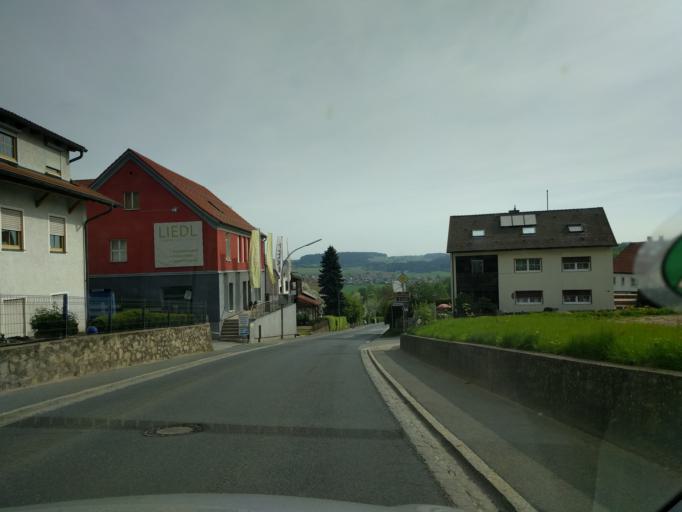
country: DE
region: Bavaria
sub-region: Upper Palatinate
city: Falkenstein
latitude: 49.0995
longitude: 12.4866
